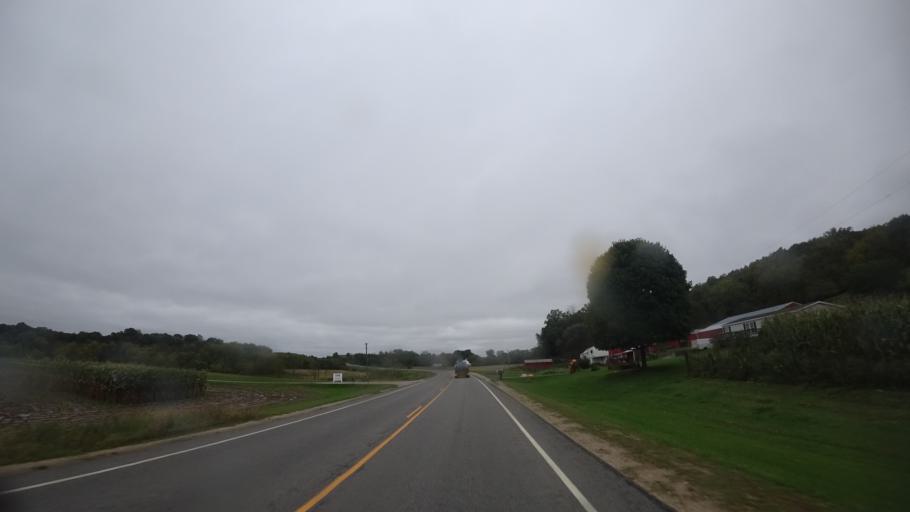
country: US
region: Wisconsin
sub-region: Crawford County
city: Prairie du Chien
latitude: 43.0256
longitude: -91.0253
